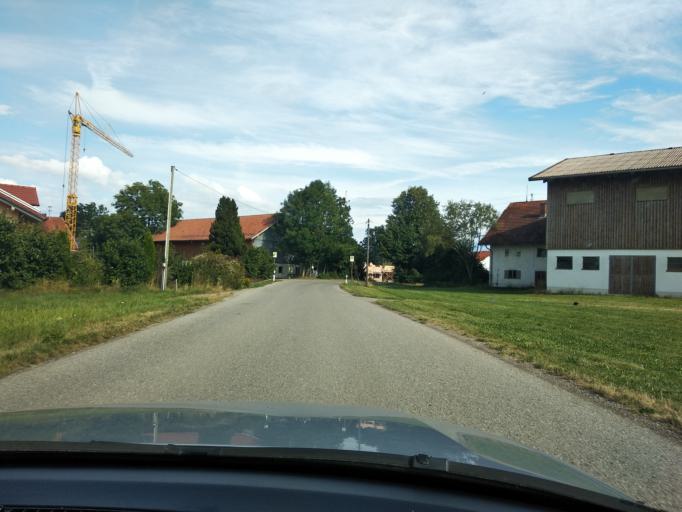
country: DE
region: Bavaria
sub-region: Swabia
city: Dietmannsried
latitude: 47.8186
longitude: 10.3208
